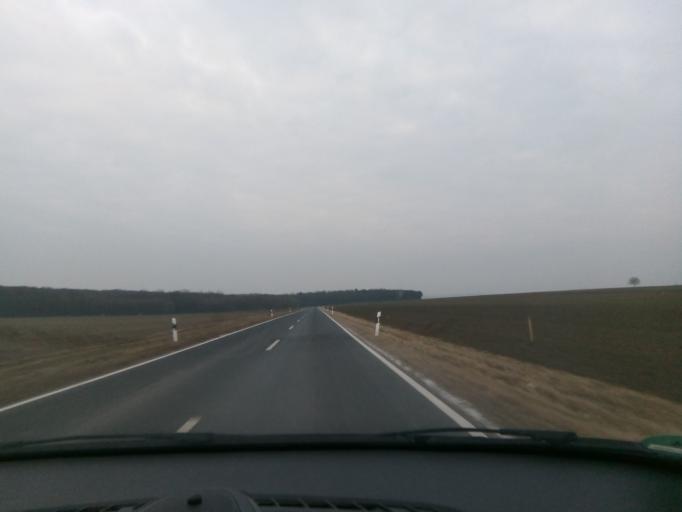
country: DE
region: Bavaria
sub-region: Regierungsbezirk Unterfranken
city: Sulzheim
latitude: 49.9483
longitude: 10.3504
